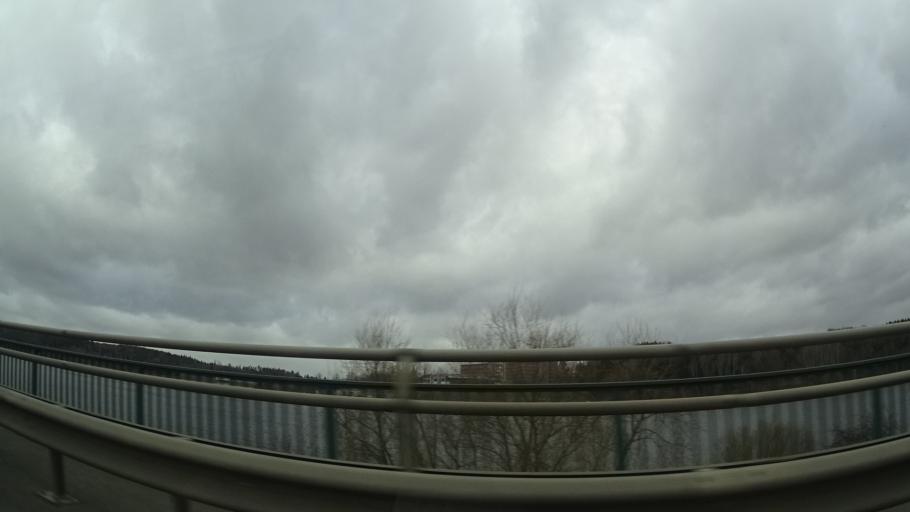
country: DE
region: Thuringia
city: Zeulenroda
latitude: 50.6632
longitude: 11.9752
